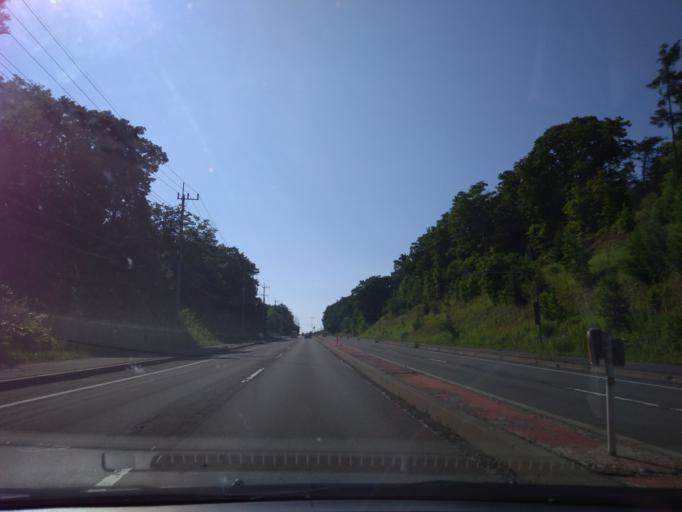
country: JP
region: Hokkaido
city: Kitahiroshima
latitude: 42.9781
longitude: 141.5081
